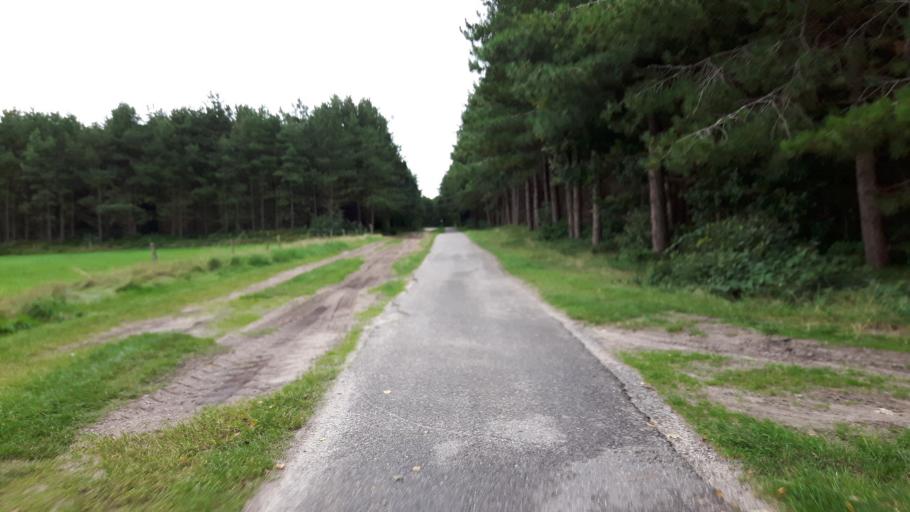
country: NL
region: Friesland
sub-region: Gemeente Ameland
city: Nes
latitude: 53.4479
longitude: 5.7126
